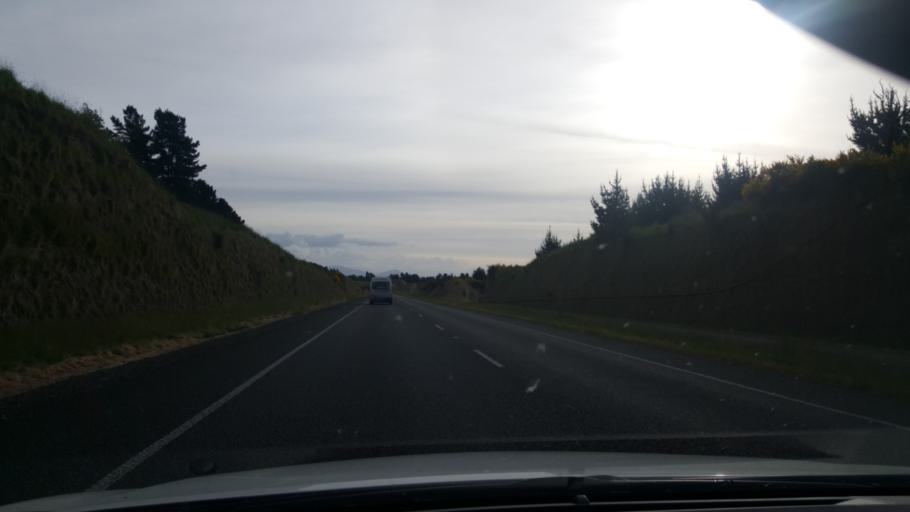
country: NZ
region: Waikato
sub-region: Taupo District
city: Taupo
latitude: -38.7307
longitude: 176.0845
